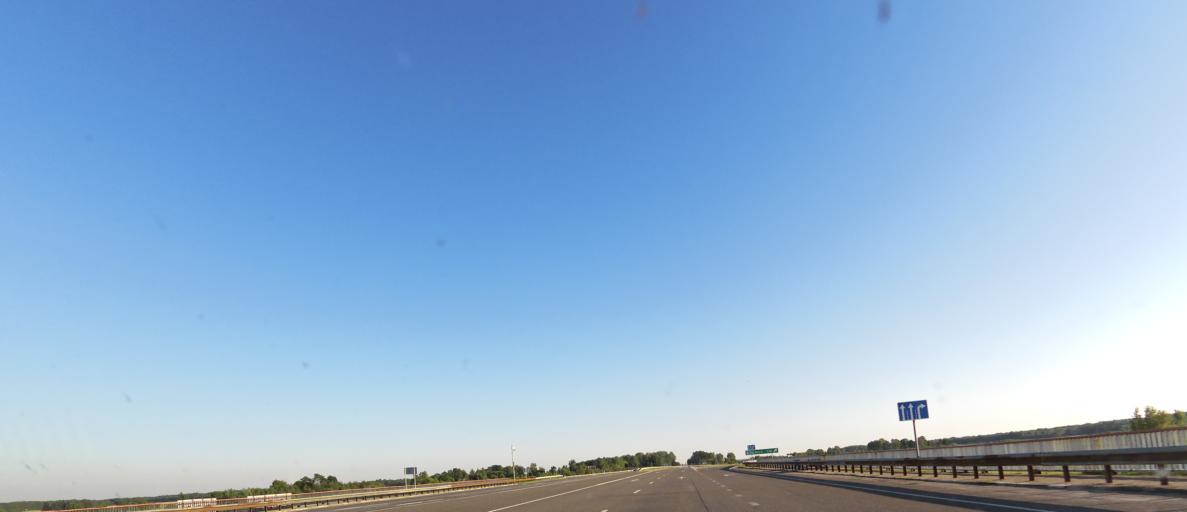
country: LT
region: Panevezys
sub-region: Panevezys City
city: Panevezys
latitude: 55.6651
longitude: 24.3629
